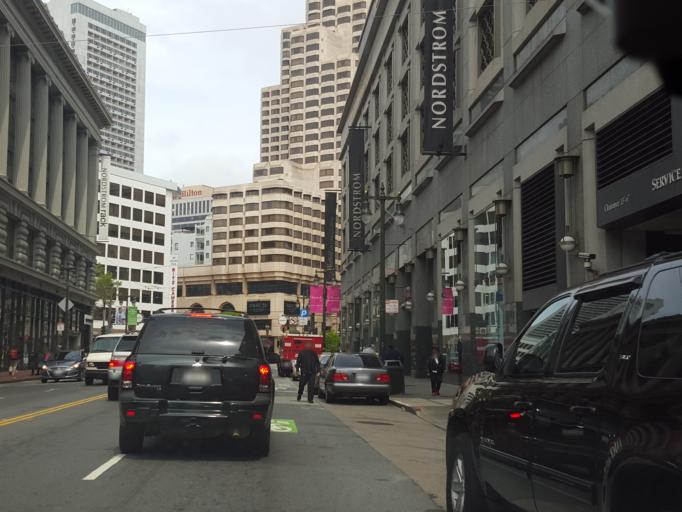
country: US
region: California
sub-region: San Francisco County
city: San Francisco
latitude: 37.7833
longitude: -122.4071
